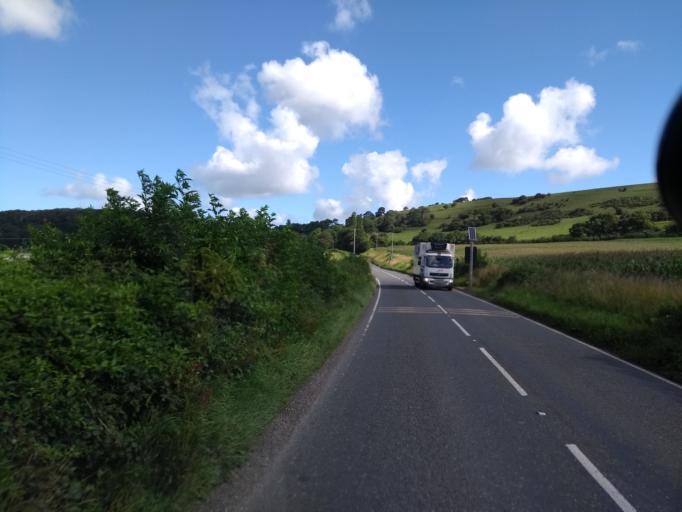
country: GB
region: England
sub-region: Somerset
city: Street
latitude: 51.1002
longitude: -2.7360
